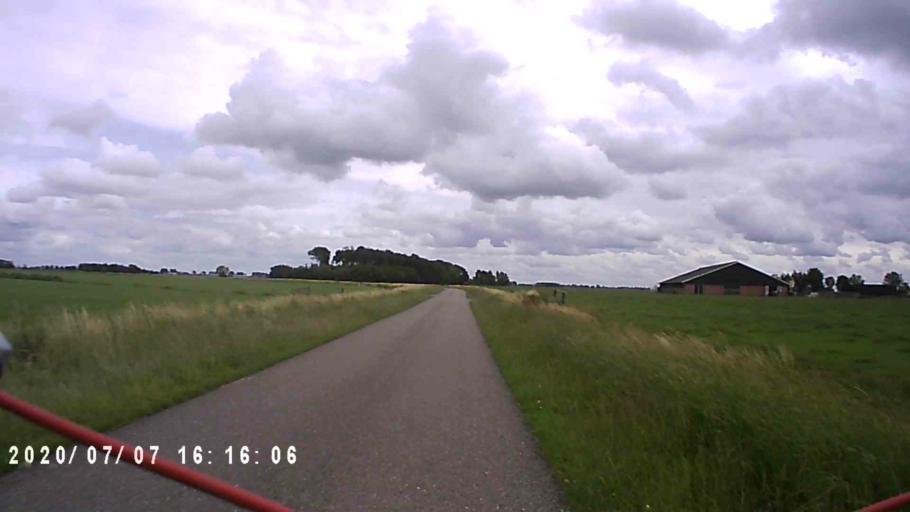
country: NL
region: Groningen
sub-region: Gemeente Winsum
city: Winsum
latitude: 53.3740
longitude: 6.5534
